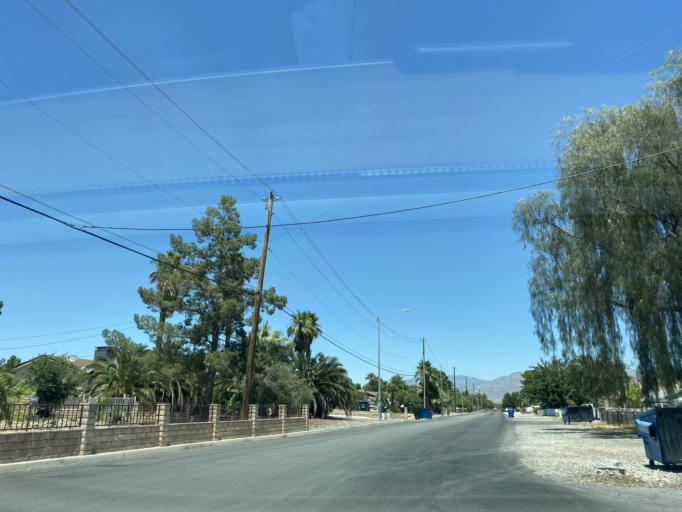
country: US
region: Nevada
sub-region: Clark County
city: Las Vegas
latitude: 36.2249
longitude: -115.2121
